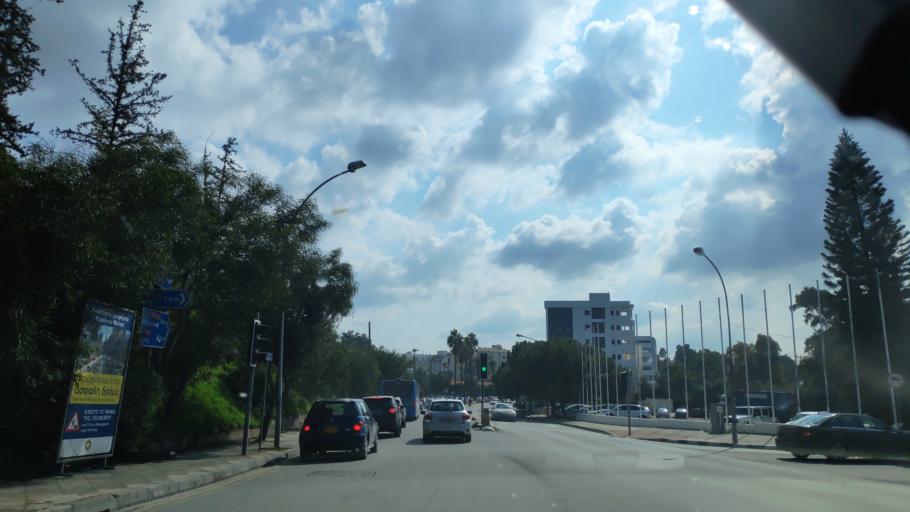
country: CY
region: Lefkosia
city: Nicosia
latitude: 35.1530
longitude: 33.3477
